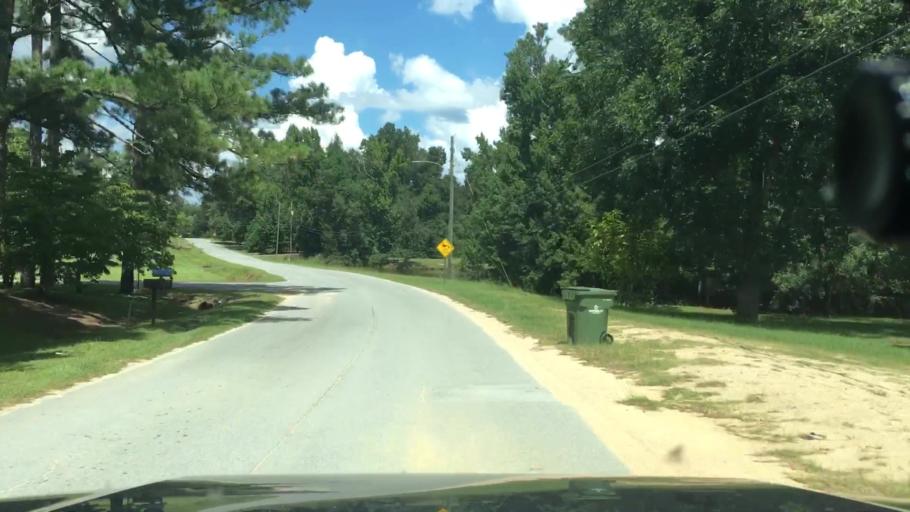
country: US
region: Georgia
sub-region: Bibb County
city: West Point
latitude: 32.8022
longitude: -83.7937
